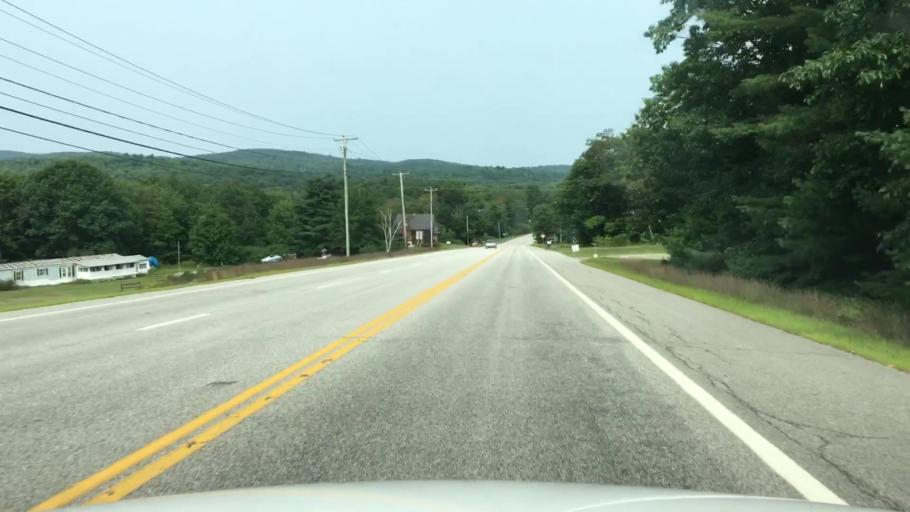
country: US
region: Maine
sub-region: Androscoggin County
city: Livermore Falls
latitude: 44.4519
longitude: -70.1683
